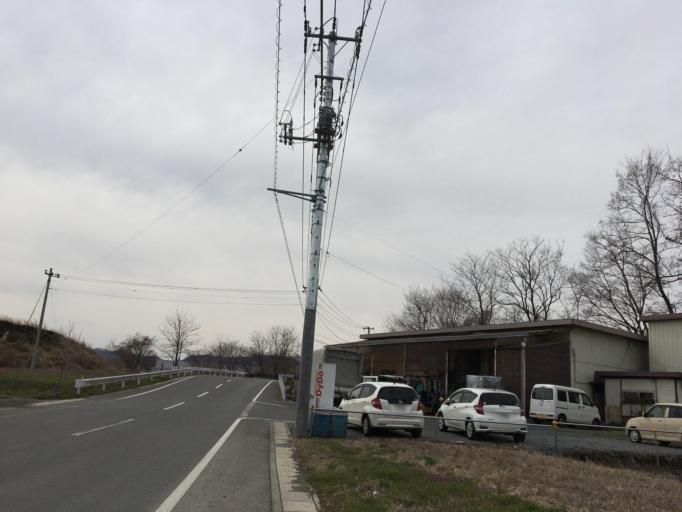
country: JP
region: Saitama
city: Kodamacho-kodamaminami
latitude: 36.1808
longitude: 139.1442
